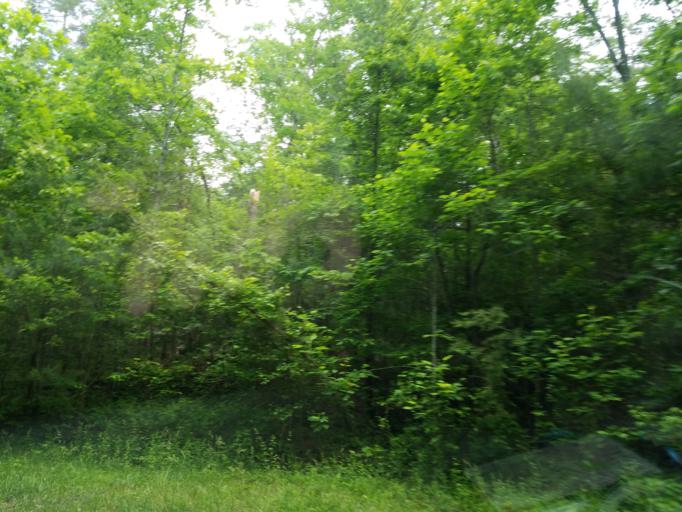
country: US
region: Georgia
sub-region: Dawson County
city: Dawsonville
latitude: 34.5803
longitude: -84.1452
